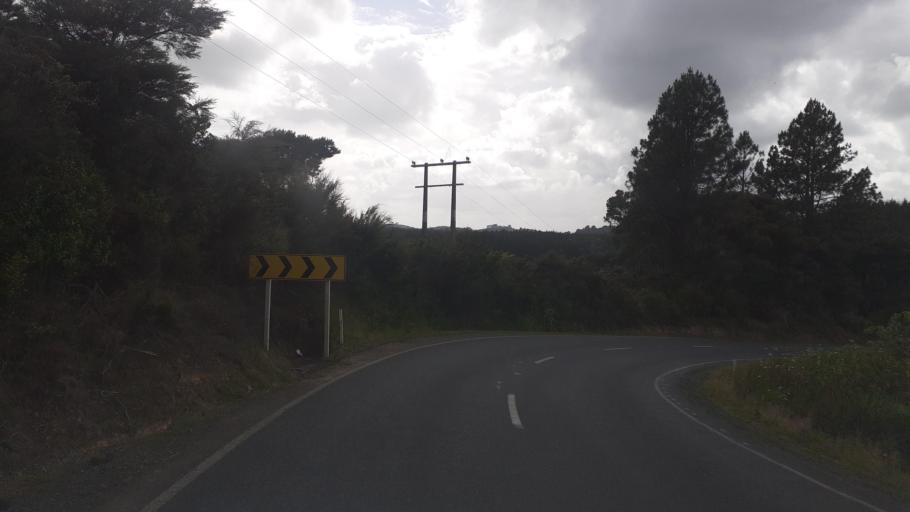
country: NZ
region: Northland
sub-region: Far North District
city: Kerikeri
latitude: -35.2249
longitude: 174.0043
